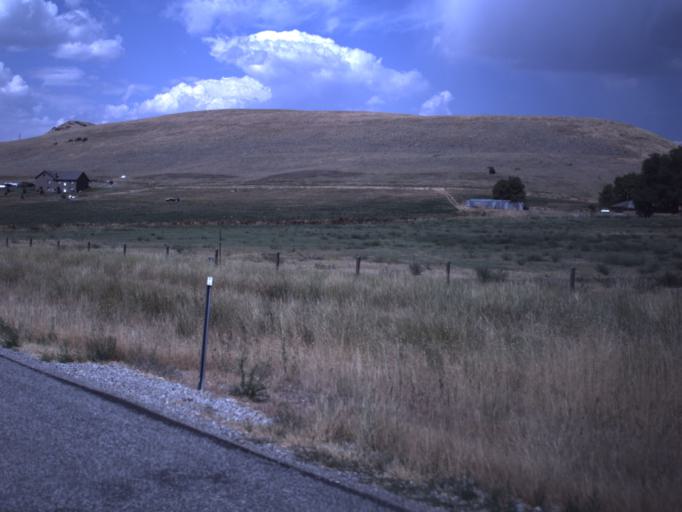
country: US
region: Utah
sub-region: Cache County
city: Mendon
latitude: 41.7892
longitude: -112.0297
